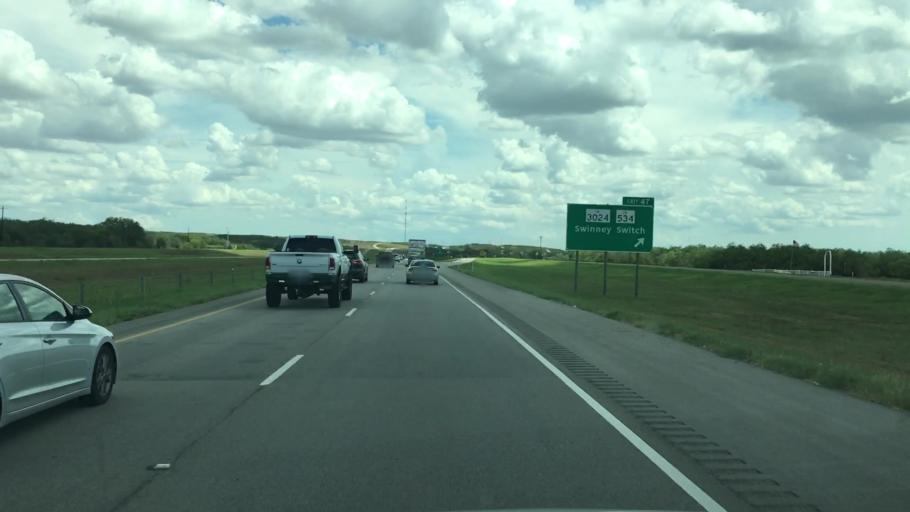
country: US
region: Texas
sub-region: Live Oak County
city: George West
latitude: 28.2672
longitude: -97.9396
